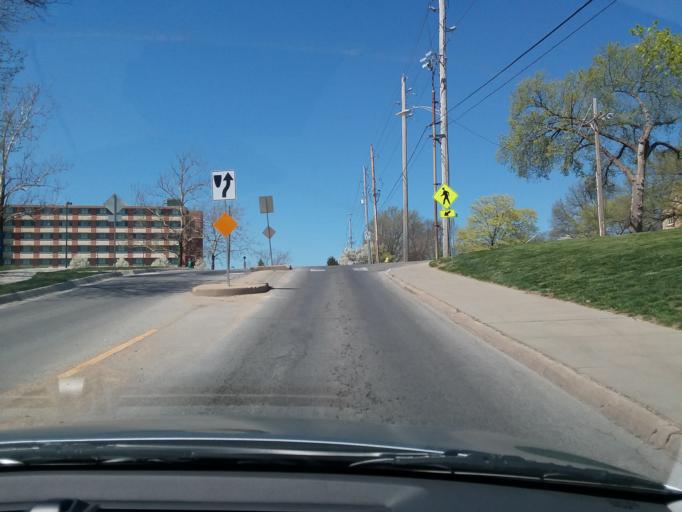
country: US
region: Kansas
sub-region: Douglas County
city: Lawrence
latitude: 38.9571
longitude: -95.2571
